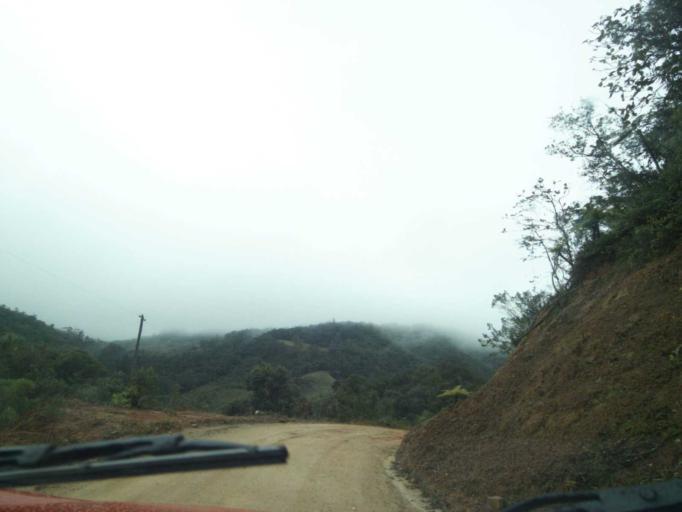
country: BR
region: Santa Catarina
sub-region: Anitapolis
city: Anitapolis
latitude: -27.9208
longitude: -49.1898
